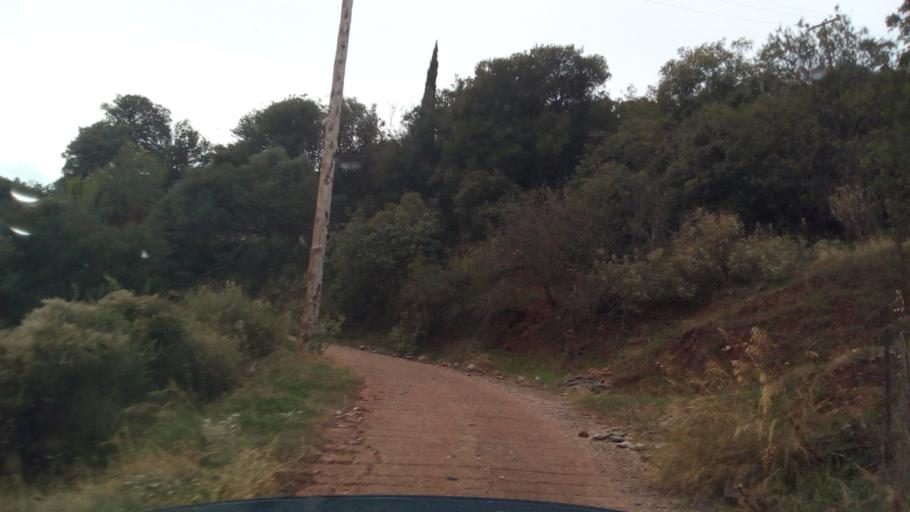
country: GR
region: West Greece
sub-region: Nomos Achaias
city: Kamarai
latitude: 38.4122
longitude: 22.0563
